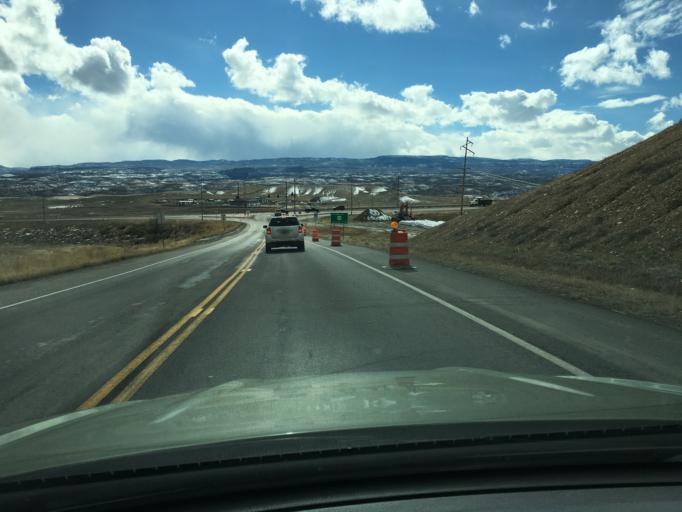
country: US
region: Colorado
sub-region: Mesa County
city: Fruitvale
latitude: 39.0160
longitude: -108.4733
